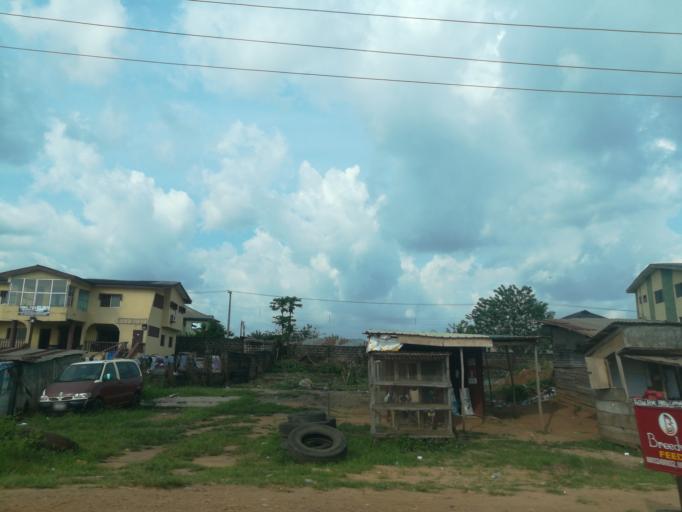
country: NG
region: Oyo
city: Ibadan
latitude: 7.3929
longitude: 3.8137
